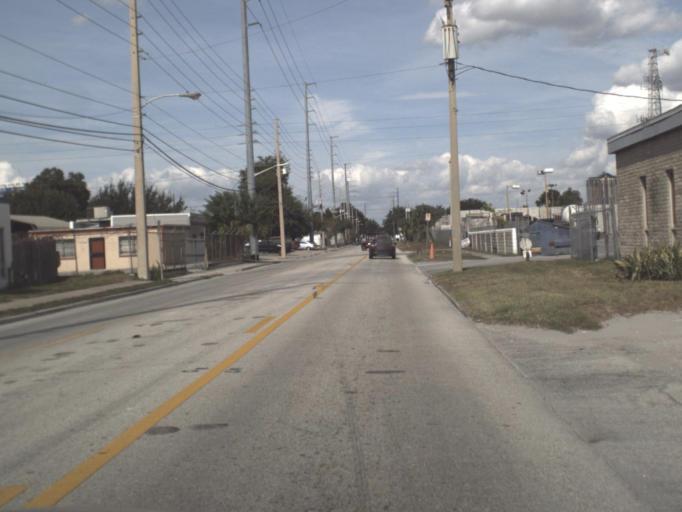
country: US
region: Florida
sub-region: Orange County
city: Orlando
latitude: 28.5230
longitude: -81.3847
